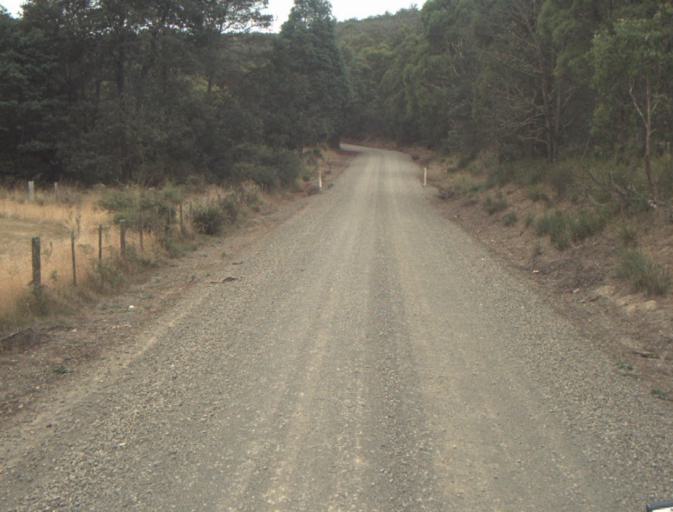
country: AU
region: Tasmania
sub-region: Northern Midlands
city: Evandale
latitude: -41.4627
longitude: 147.4957
